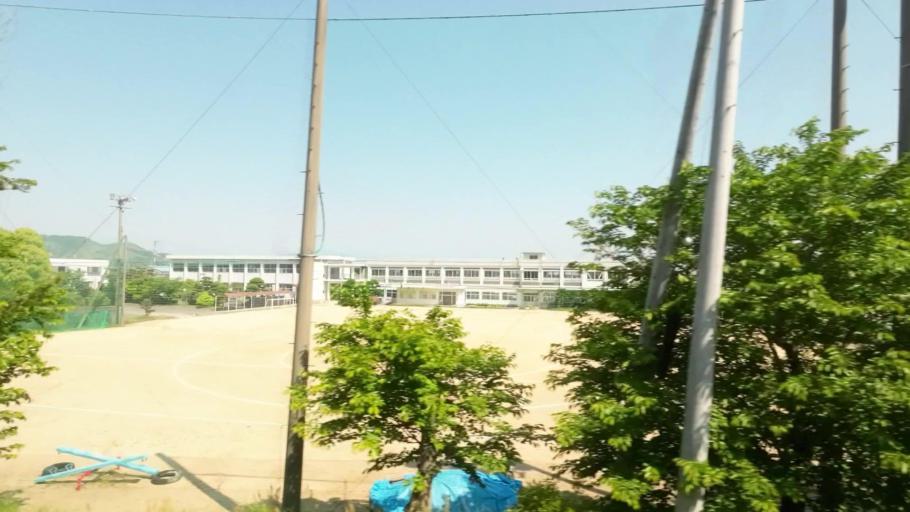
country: JP
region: Ehime
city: Niihama
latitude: 33.9615
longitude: 133.4375
